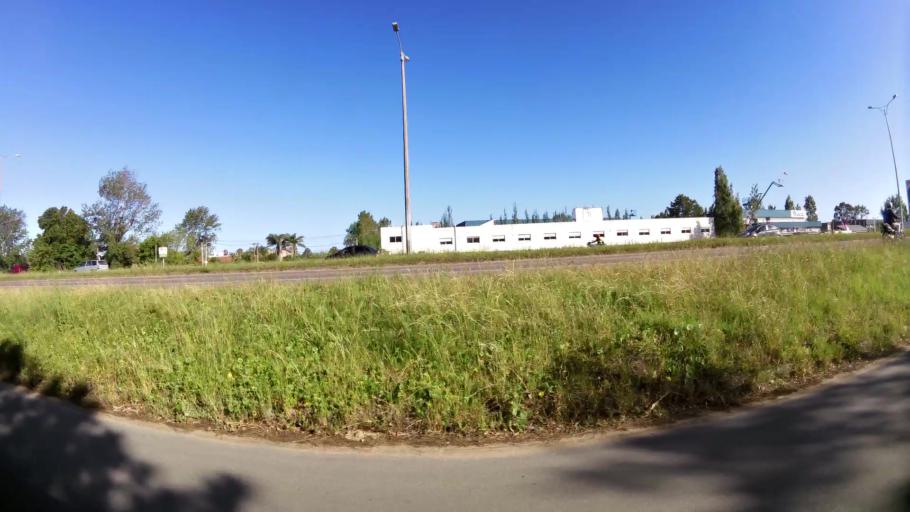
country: UY
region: Canelones
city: Barra de Carrasco
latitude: -34.8705
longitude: -56.0280
